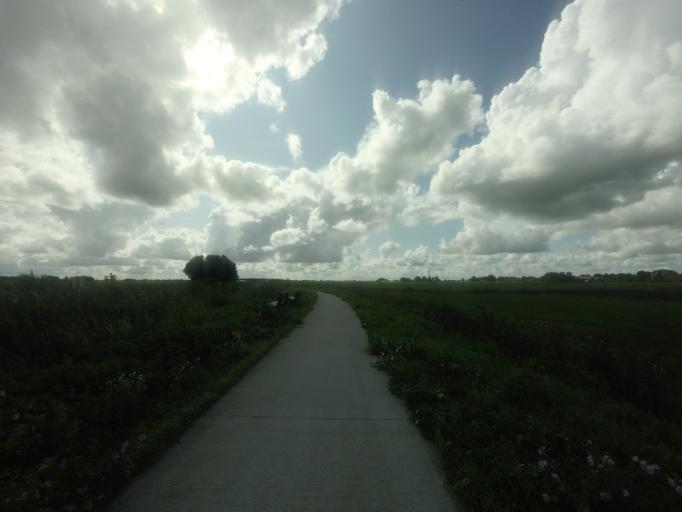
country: NL
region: Friesland
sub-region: Gemeente Littenseradiel
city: Makkum
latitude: 53.0905
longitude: 5.7096
